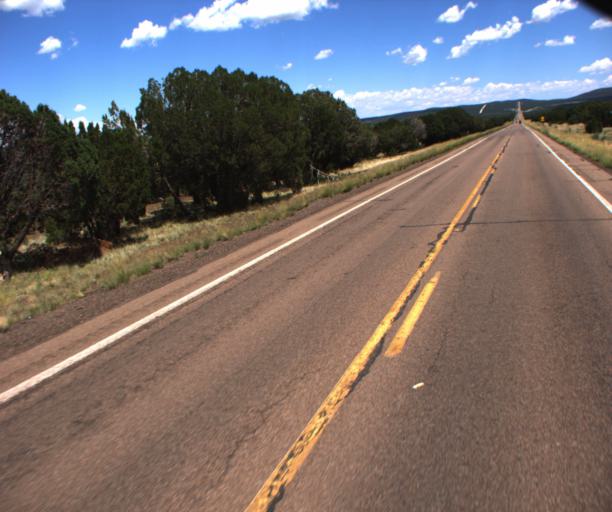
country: US
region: Arizona
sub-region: Navajo County
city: White Mountain Lake
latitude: 34.2779
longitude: -109.8829
